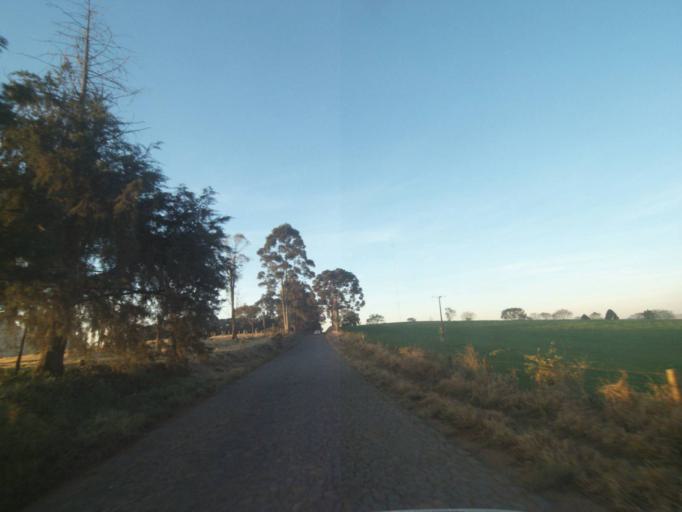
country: BR
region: Parana
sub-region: Tibagi
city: Tibagi
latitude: -24.5322
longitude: -50.4592
